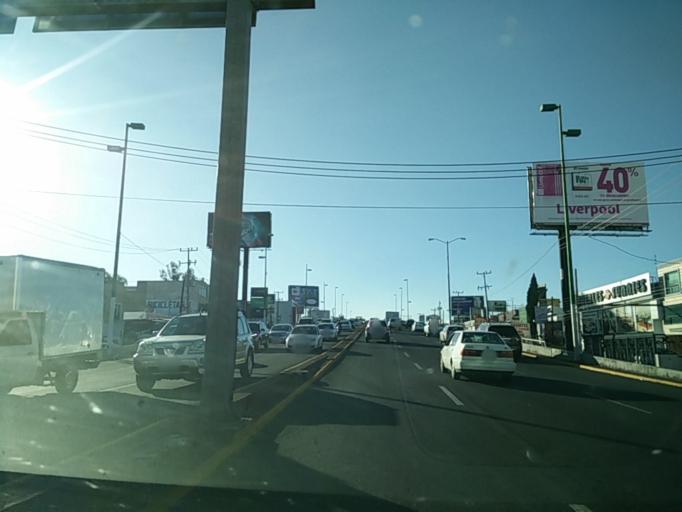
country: MX
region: Jalisco
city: Guadalajara
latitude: 20.6784
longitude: -103.4191
